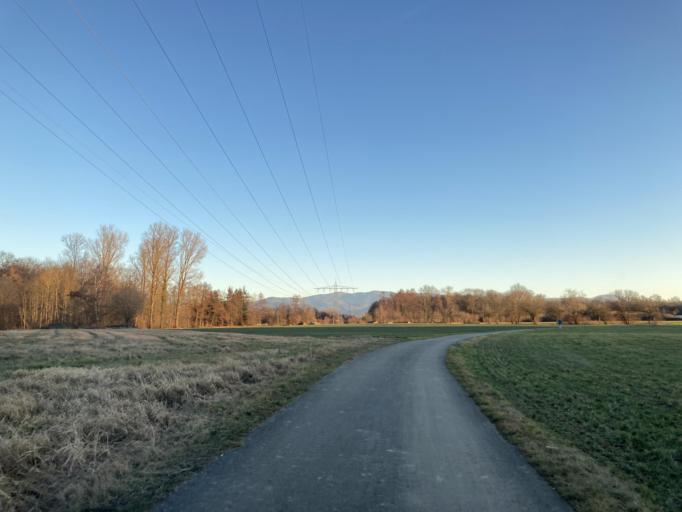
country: DE
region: Baden-Wuerttemberg
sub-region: Freiburg Region
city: Umkirch
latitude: 48.0482
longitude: 7.7685
